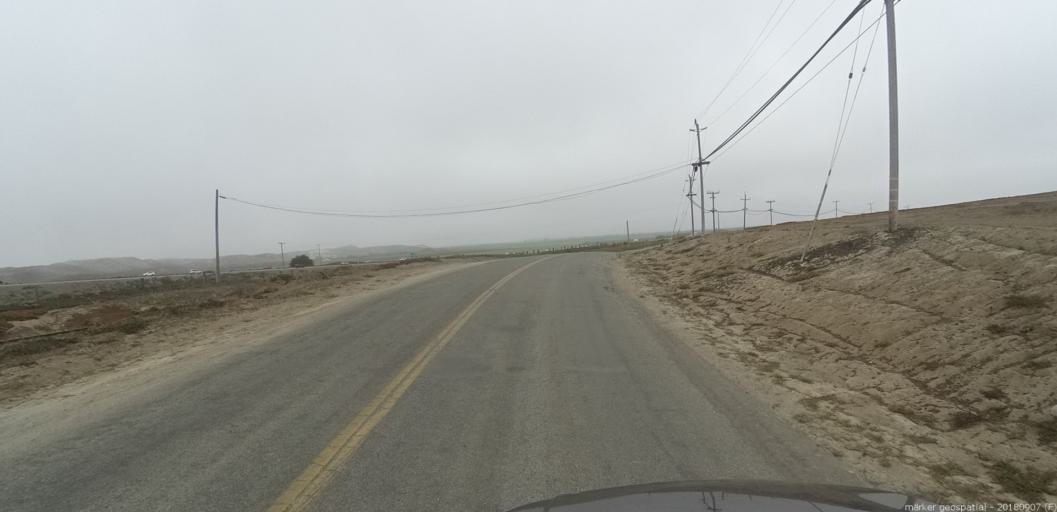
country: US
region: California
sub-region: Monterey County
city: Marina
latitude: 36.7151
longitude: -121.7923
